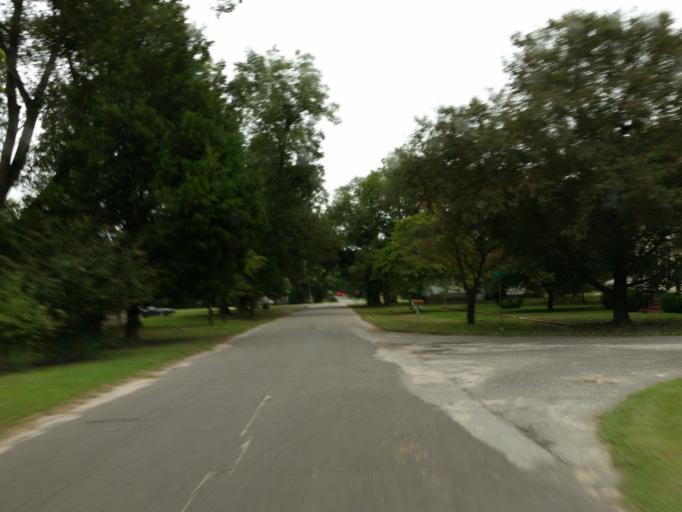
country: US
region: Georgia
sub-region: Dooly County
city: Unadilla
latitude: 32.2635
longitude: -83.7389
